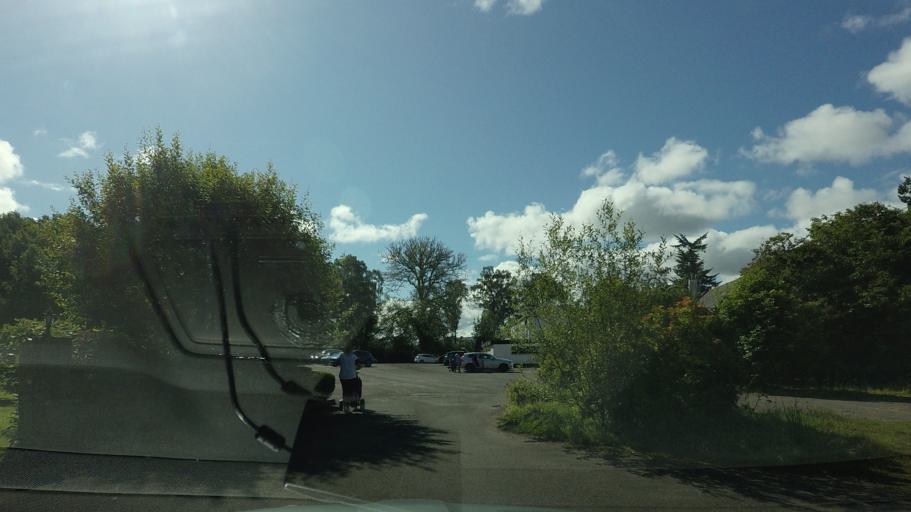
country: GB
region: Scotland
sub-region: Stirling
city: Killearn
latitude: 56.0678
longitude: -4.4802
